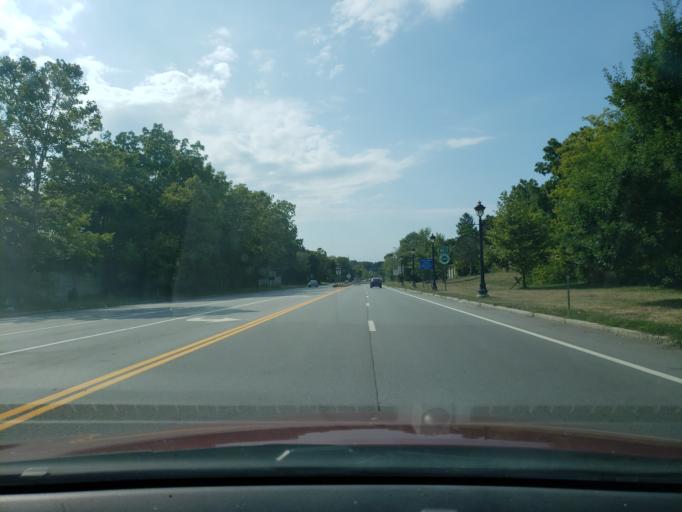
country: US
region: New York
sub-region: Monroe County
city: Irondequoit
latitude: 43.2499
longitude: -77.6151
